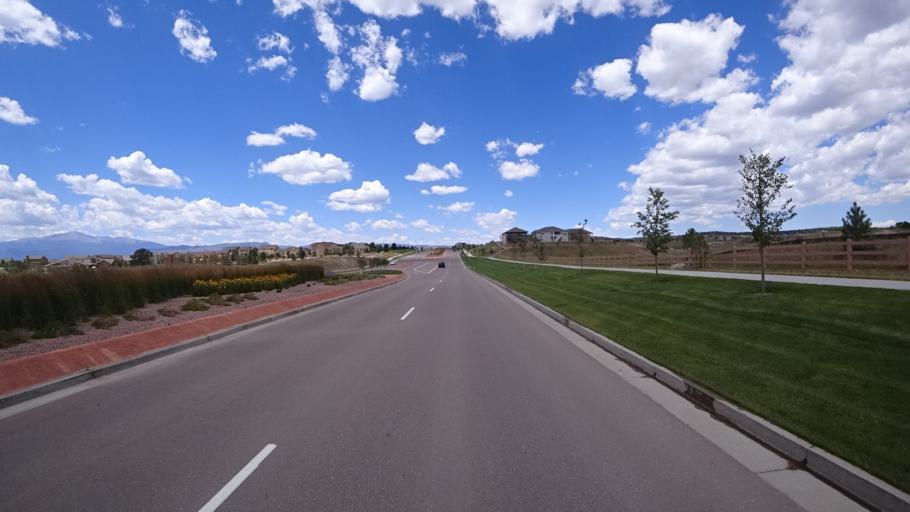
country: US
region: Colorado
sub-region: El Paso County
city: Black Forest
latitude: 38.9603
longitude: -104.7096
